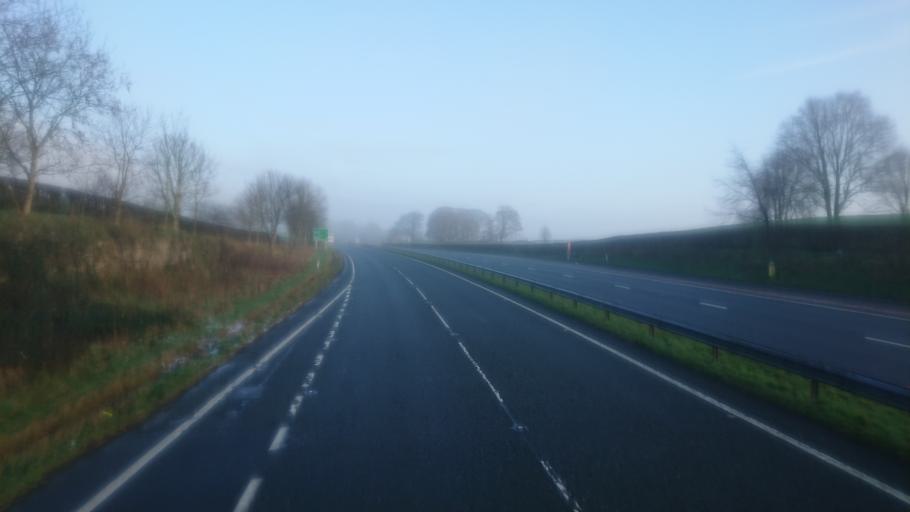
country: GB
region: England
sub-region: Cumbria
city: Milnthorpe
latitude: 54.2665
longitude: -2.7746
